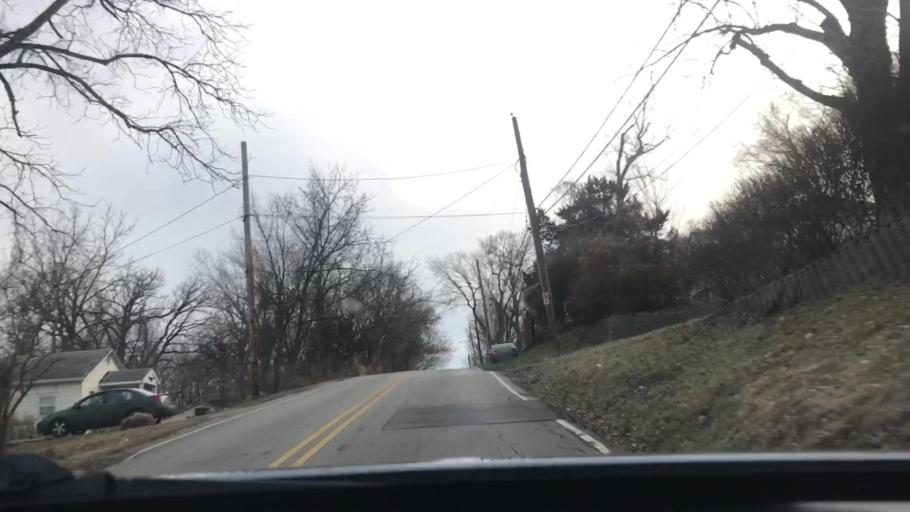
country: US
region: Missouri
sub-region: Jackson County
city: Independence
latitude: 39.0709
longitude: -94.4428
